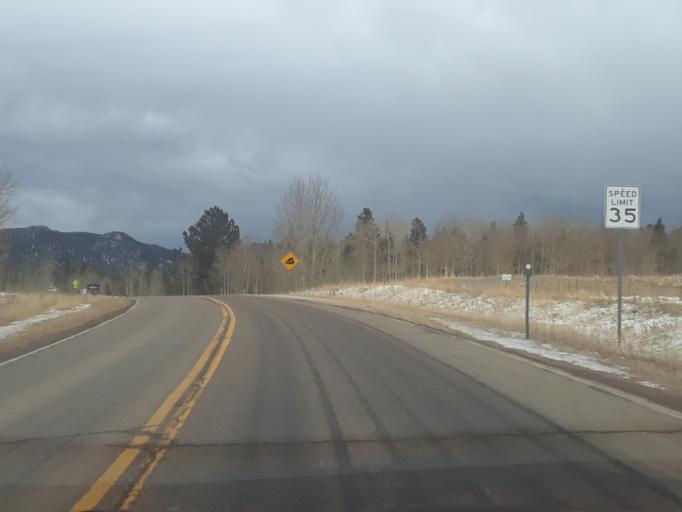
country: US
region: Colorado
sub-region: Gilpin County
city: Central City
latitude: 39.8383
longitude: -105.4786
